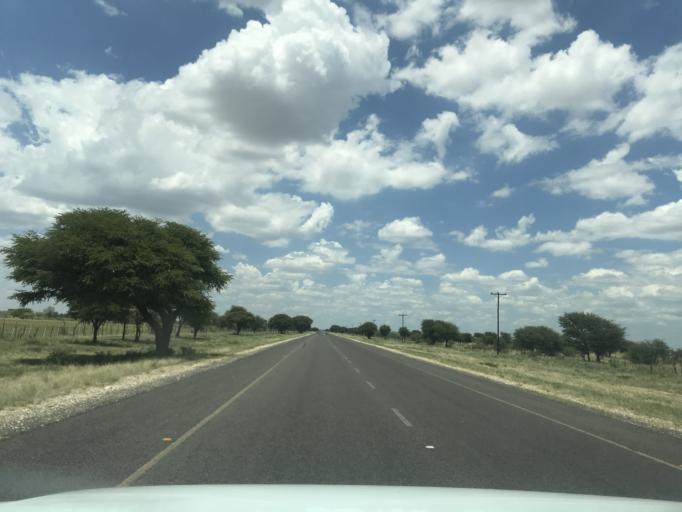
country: BW
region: South East
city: Janeng
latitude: -25.6888
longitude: 25.1302
